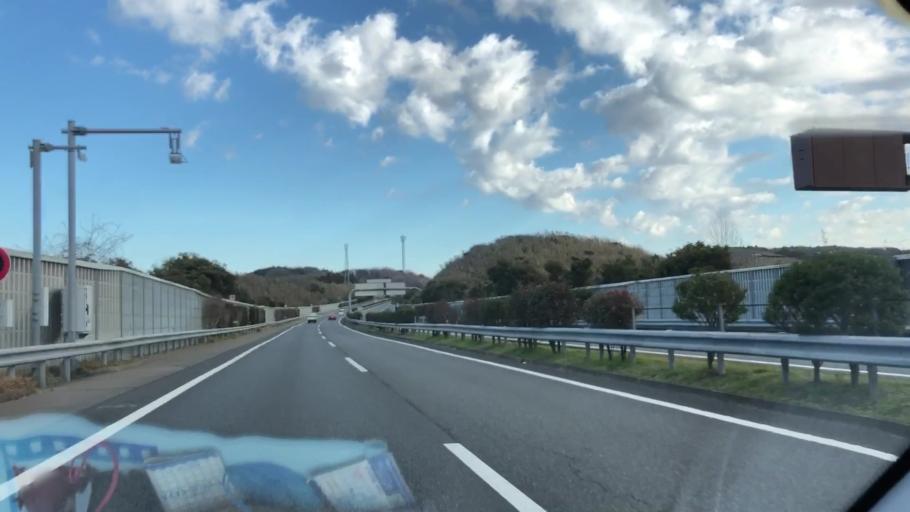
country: JP
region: Chiba
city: Kisarazu
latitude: 35.3614
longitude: 139.9568
